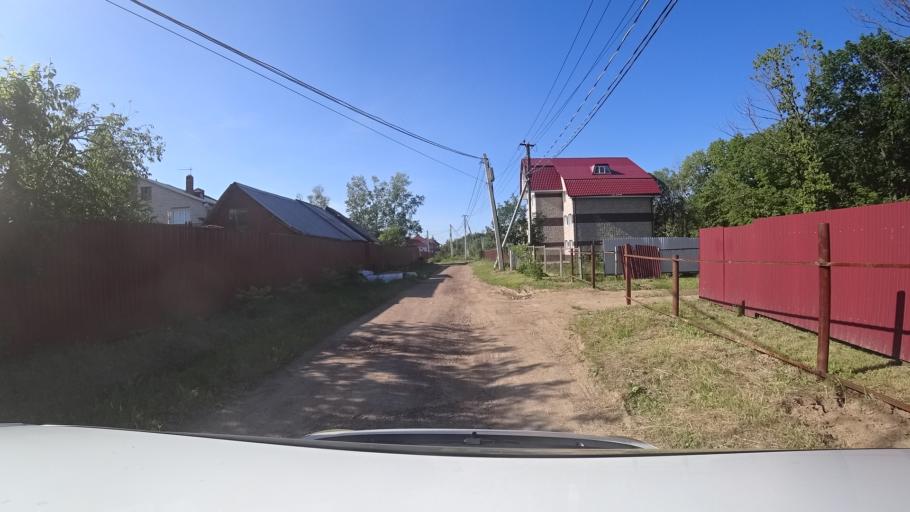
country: RU
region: Khabarovsk Krai
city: Topolevo
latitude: 48.5411
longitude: 135.1791
